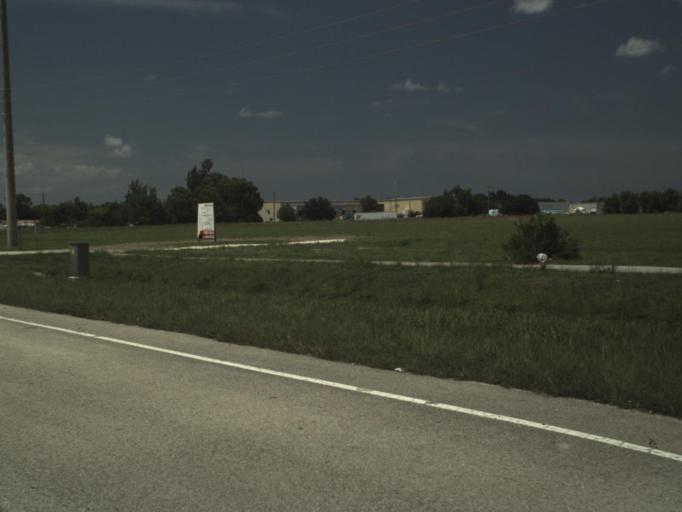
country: US
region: Florida
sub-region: Martin County
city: Port Salerno
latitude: 27.1477
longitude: -80.2156
